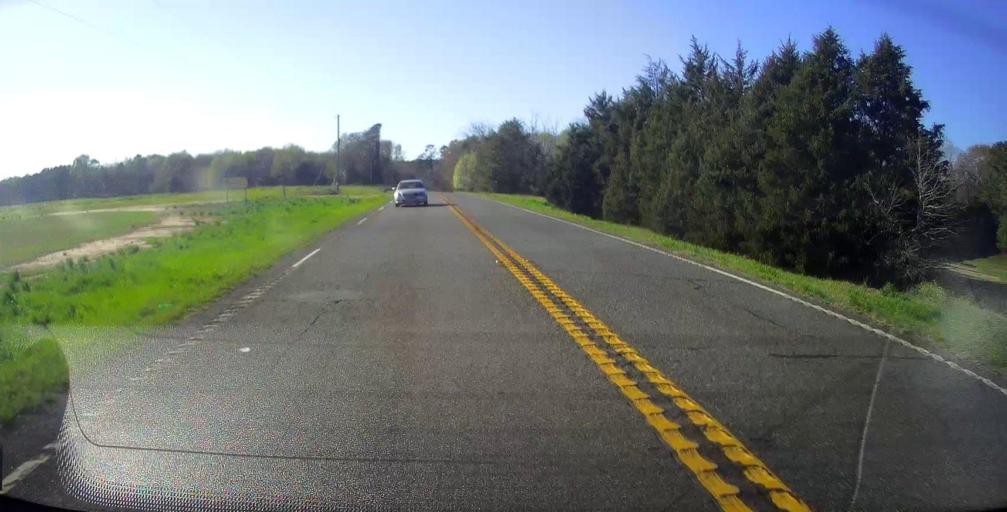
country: US
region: Georgia
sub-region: Macon County
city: Marshallville
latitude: 32.4469
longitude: -83.9036
